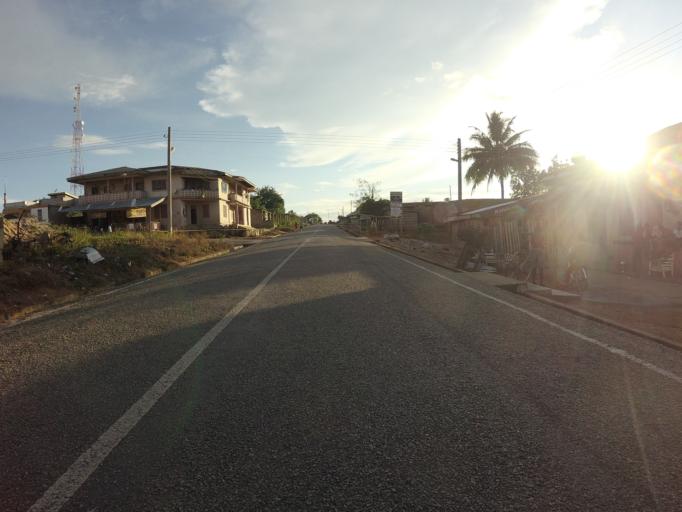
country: GH
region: Ashanti
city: Tafo
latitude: 6.9413
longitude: -1.6764
